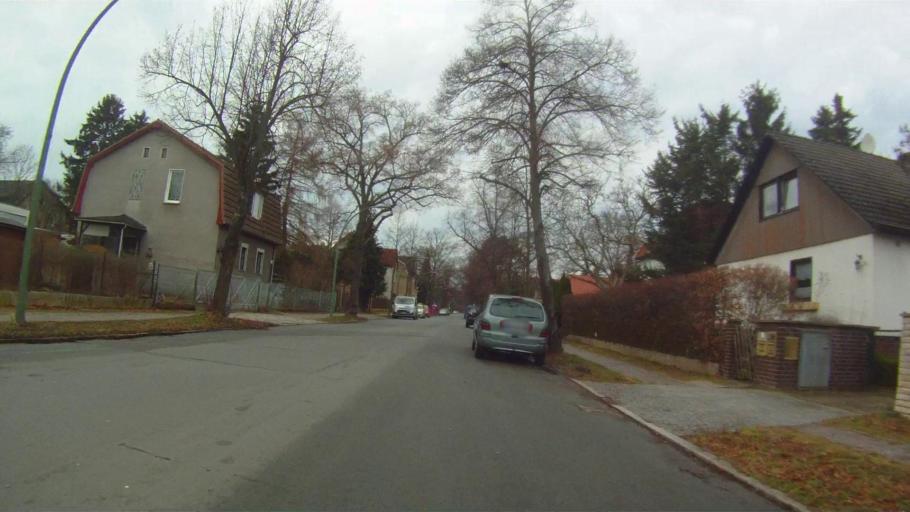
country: DE
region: Berlin
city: Lichtenrade
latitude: 52.3821
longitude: 13.4072
